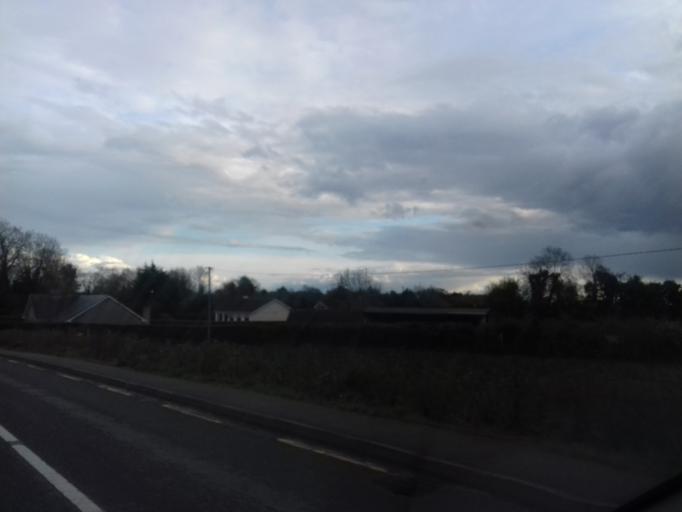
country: IE
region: Ulster
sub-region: An Cabhan
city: Ballyconnell
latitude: 54.1049
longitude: -7.5699
